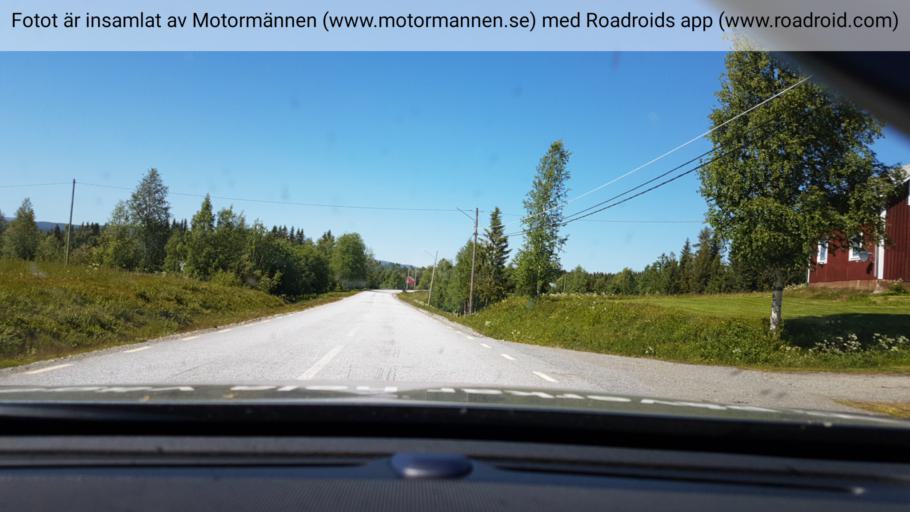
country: SE
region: Vaesterbotten
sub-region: Vilhelmina Kommun
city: Sjoberg
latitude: 64.8323
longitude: 15.9383
